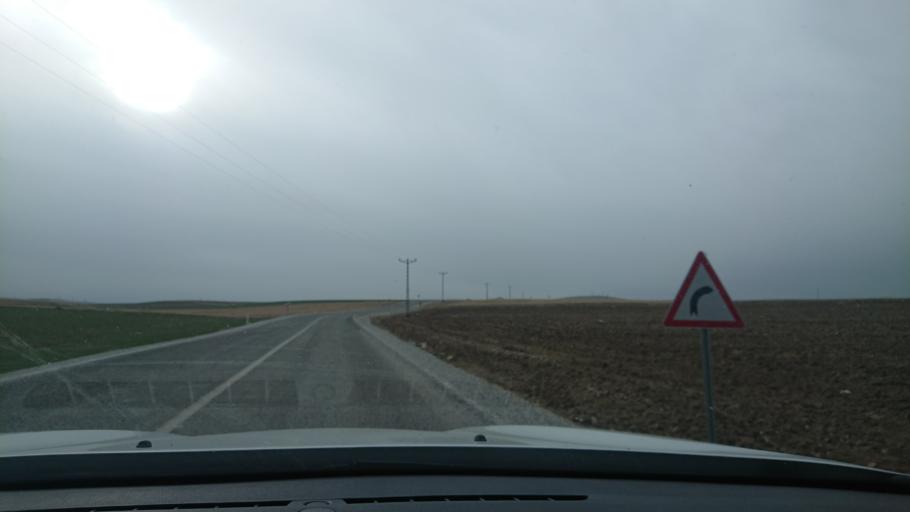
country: TR
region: Aksaray
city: Agacoren
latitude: 38.9239
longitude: 33.9473
